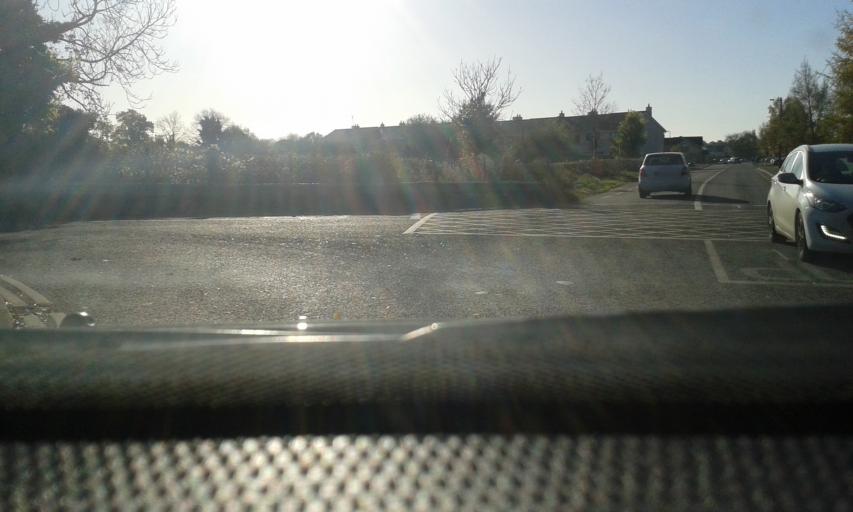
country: IE
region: Leinster
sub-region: Kildare
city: Monasterevin
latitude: 53.1468
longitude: -7.0555
